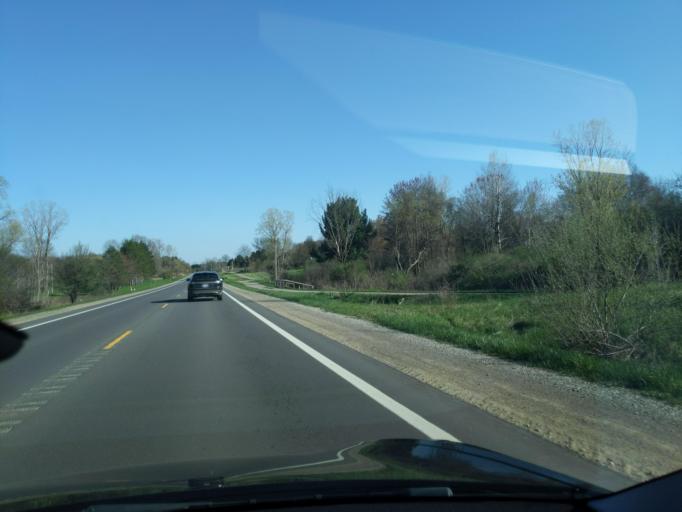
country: US
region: Michigan
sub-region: Washtenaw County
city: Chelsea
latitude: 42.3580
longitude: -84.0590
